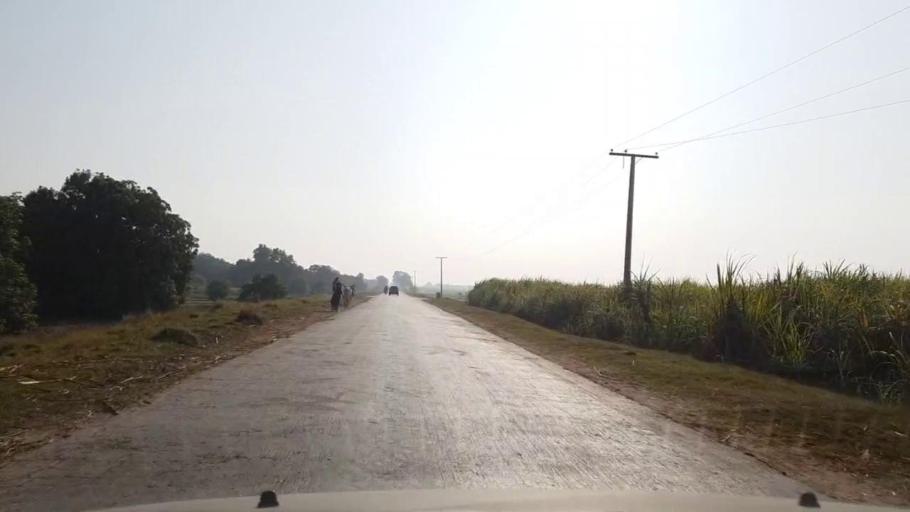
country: PK
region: Sindh
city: Matiari
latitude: 25.5623
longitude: 68.5259
